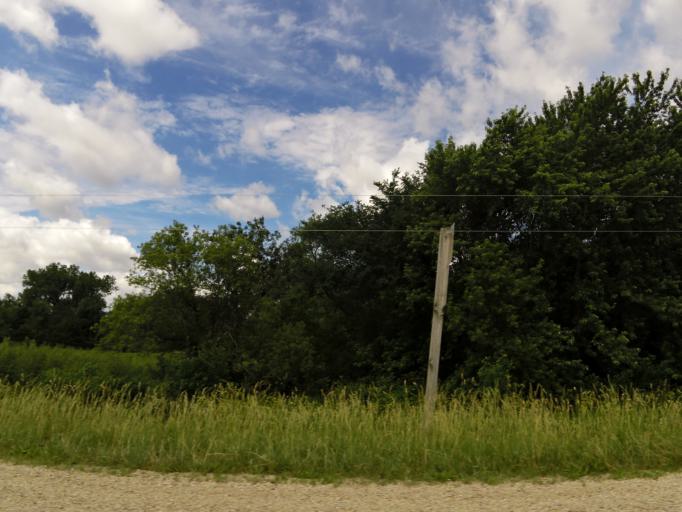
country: US
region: Iowa
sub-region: Chickasaw County
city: New Hampton
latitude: 43.2010
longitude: -92.2983
